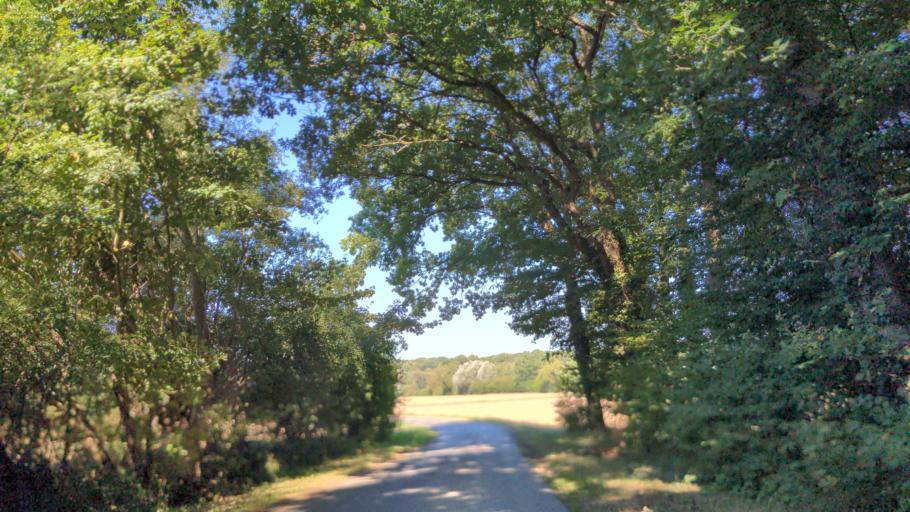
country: DE
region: Schleswig-Holstein
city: Gross Disnack
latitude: 53.7470
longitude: 10.6903
